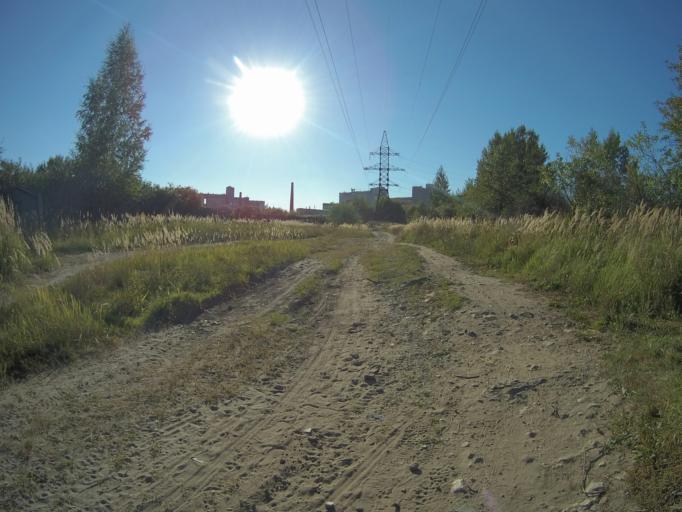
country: RU
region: Vladimir
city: Vladimir
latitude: 56.1004
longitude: 40.3757
